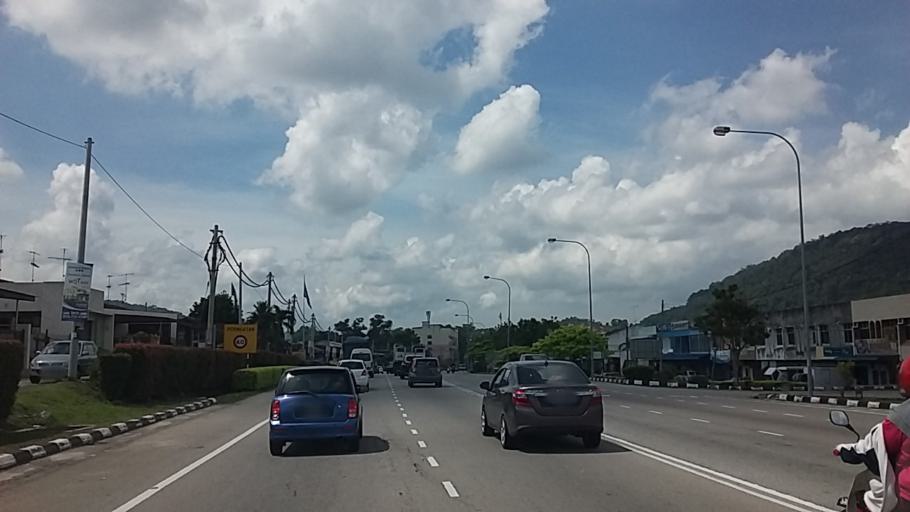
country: MY
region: Johor
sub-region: Daerah Batu Pahat
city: Batu Pahat
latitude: 1.8444
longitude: 102.9420
